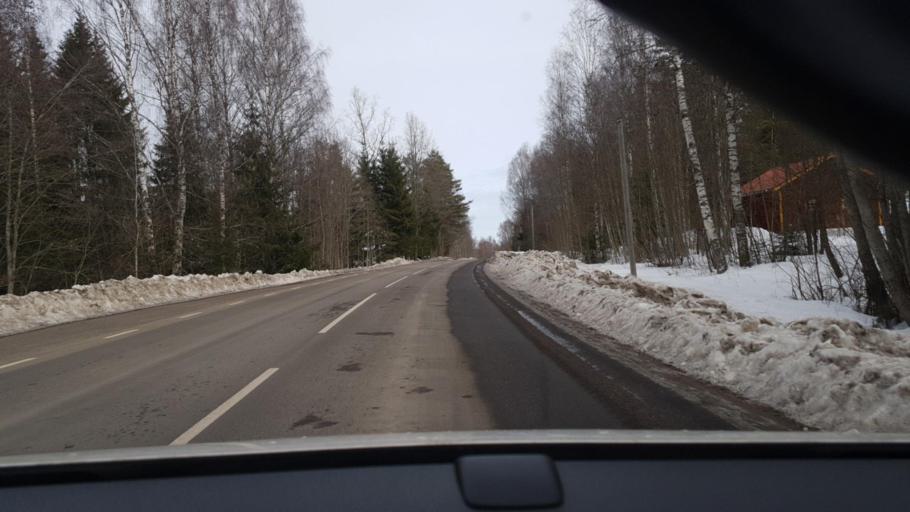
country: SE
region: Vaermland
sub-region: Eda Kommun
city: Amotfors
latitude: 59.7021
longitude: 12.4316
